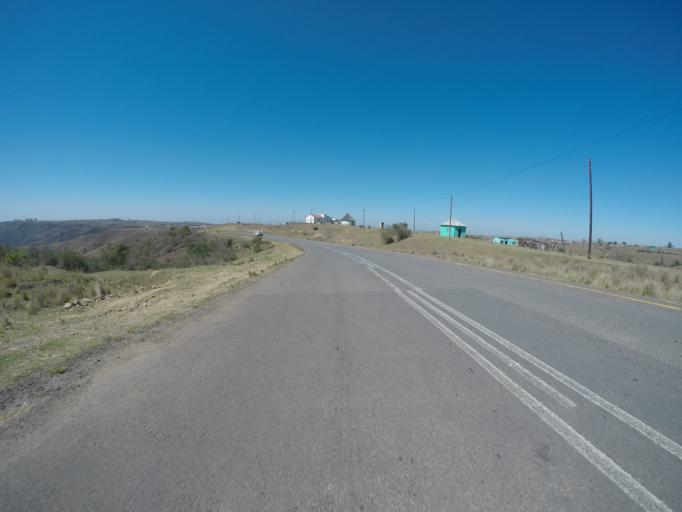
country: ZA
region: Eastern Cape
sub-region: OR Tambo District Municipality
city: Mthatha
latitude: -31.8969
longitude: 28.9442
